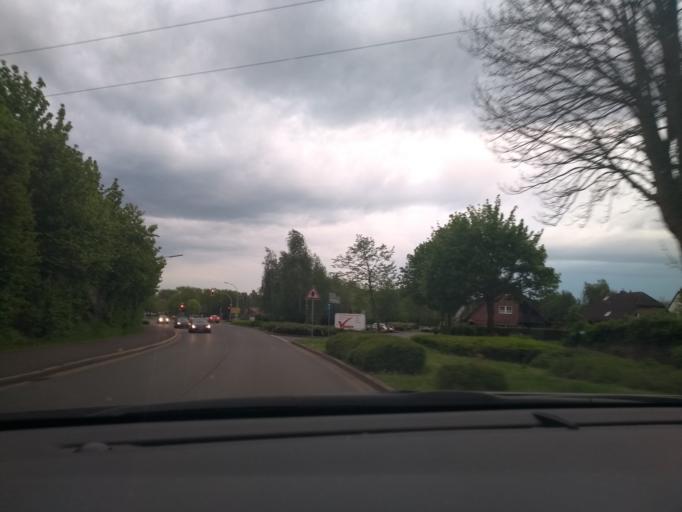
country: DE
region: North Rhine-Westphalia
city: Selm
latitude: 51.6600
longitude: 7.4666
